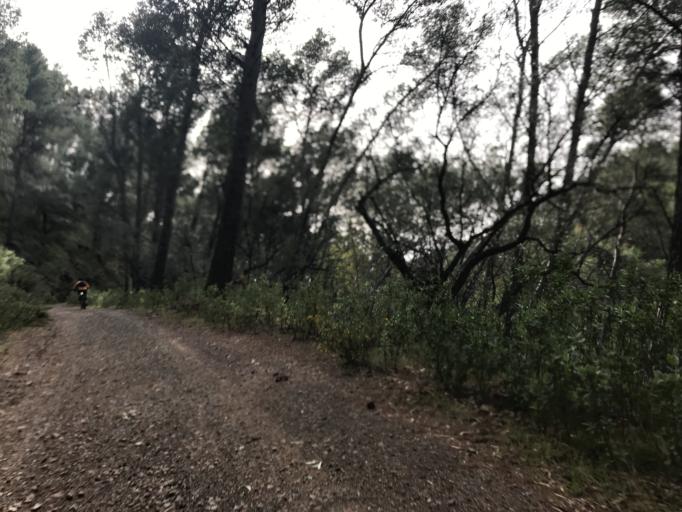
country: ES
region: Andalusia
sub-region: Provincia de Malaga
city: Malaga
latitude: 36.8057
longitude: -4.3984
